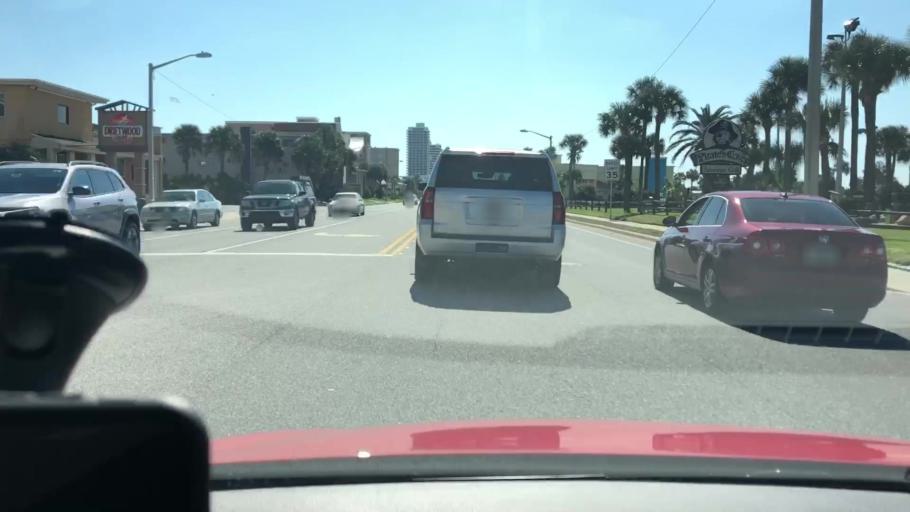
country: US
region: Florida
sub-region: Volusia County
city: Ormond Beach
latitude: 29.2753
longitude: -81.0317
